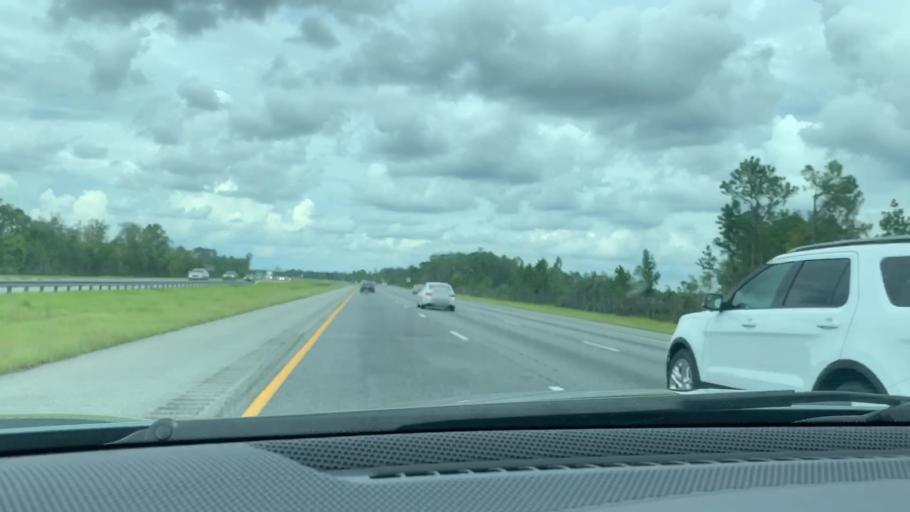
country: US
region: Georgia
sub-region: McIntosh County
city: Darien
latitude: 31.4083
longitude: -81.4453
